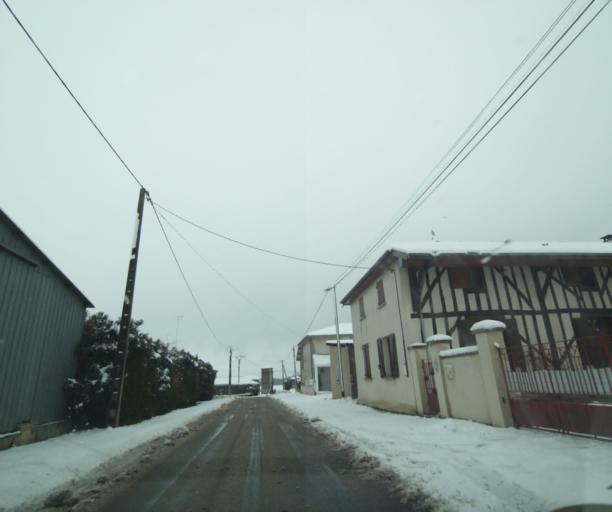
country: FR
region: Champagne-Ardenne
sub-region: Departement de la Haute-Marne
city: Montier-en-Der
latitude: 48.5100
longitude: 4.7808
